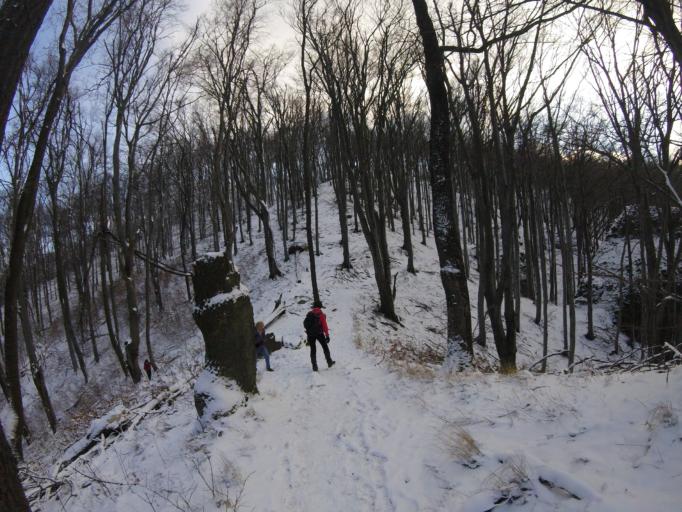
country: HU
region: Pest
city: Pilisszentkereszt
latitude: 47.7214
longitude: 18.9017
